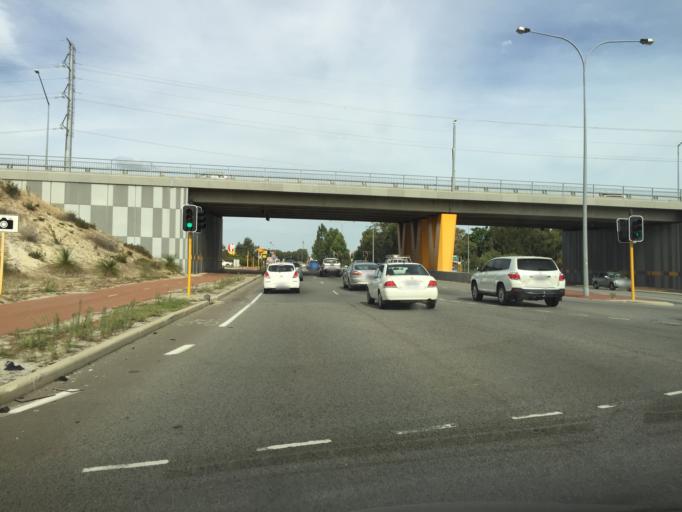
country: AU
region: Western Australia
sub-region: Canning
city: Willetton
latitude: -32.0688
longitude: 115.8894
